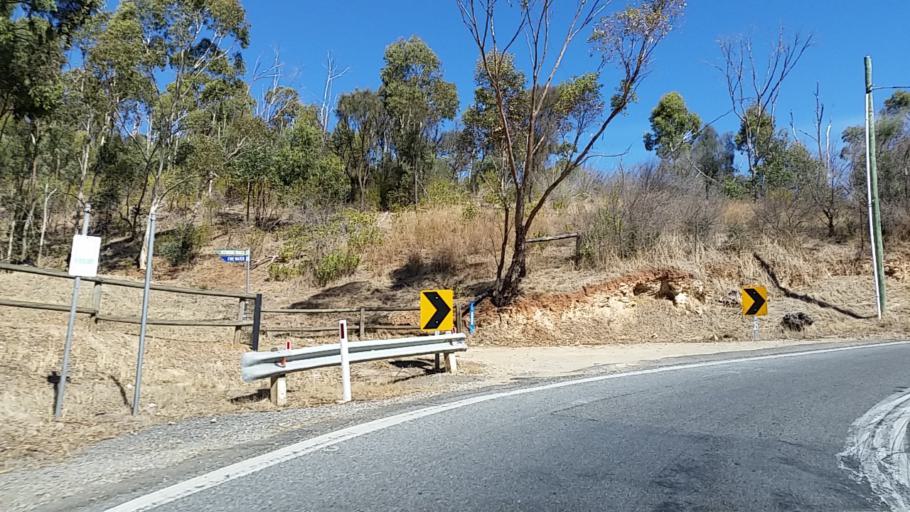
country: AU
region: South Australia
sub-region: Burnside
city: Beaumont
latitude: -34.9434
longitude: 138.6724
